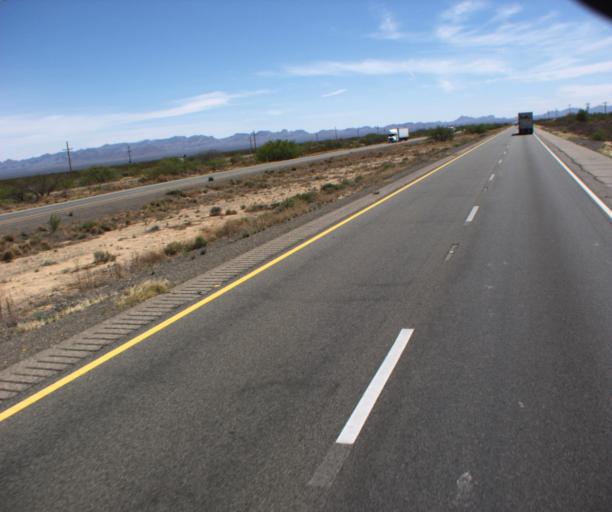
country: US
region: Arizona
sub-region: Cochise County
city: Willcox
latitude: 32.2936
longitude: -109.3384
